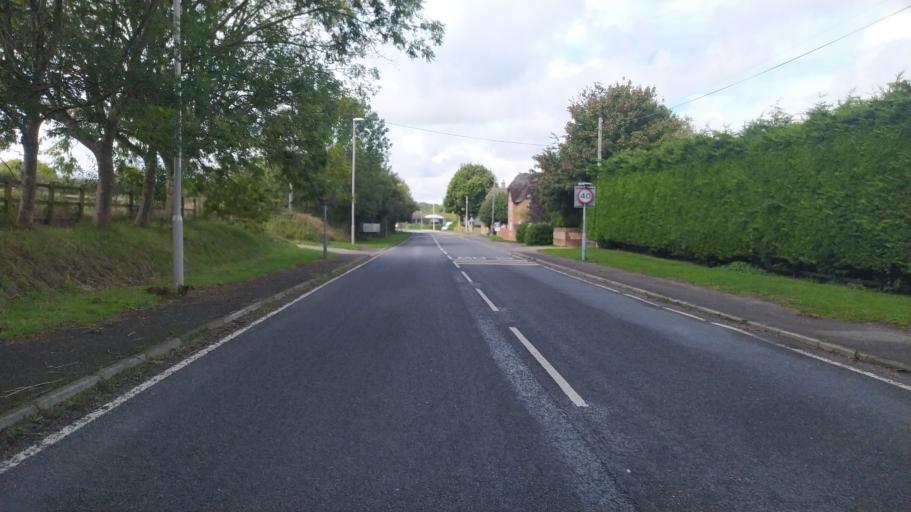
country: GB
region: England
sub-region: Dorset
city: Sturminster Newton
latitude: 50.9195
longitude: -2.3150
